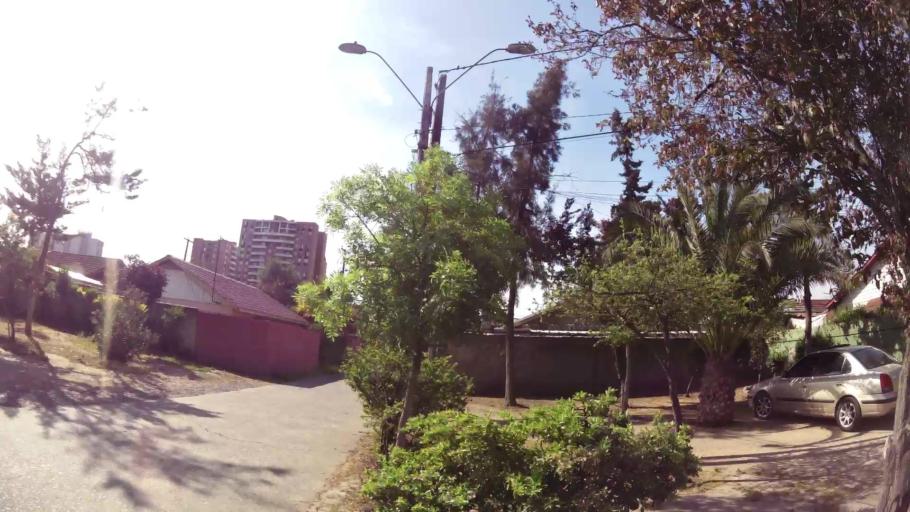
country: CL
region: Santiago Metropolitan
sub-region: Provincia de Santiago
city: La Pintana
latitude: -33.5288
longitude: -70.5940
